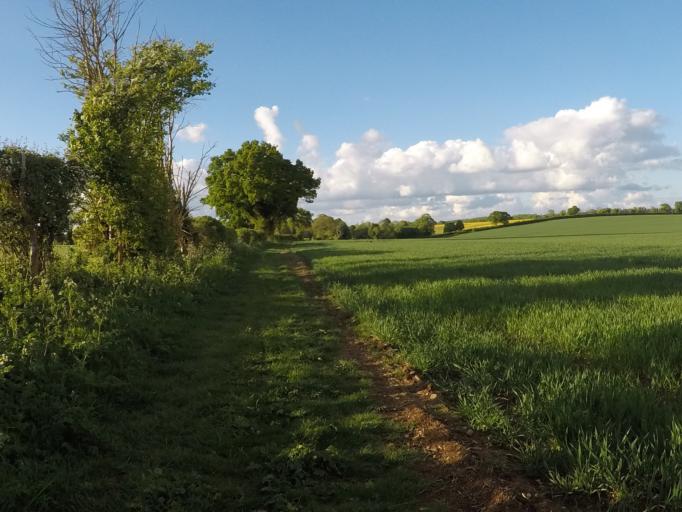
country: GB
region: England
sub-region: Oxfordshire
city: Stonesfield
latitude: 51.8629
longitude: -1.4548
